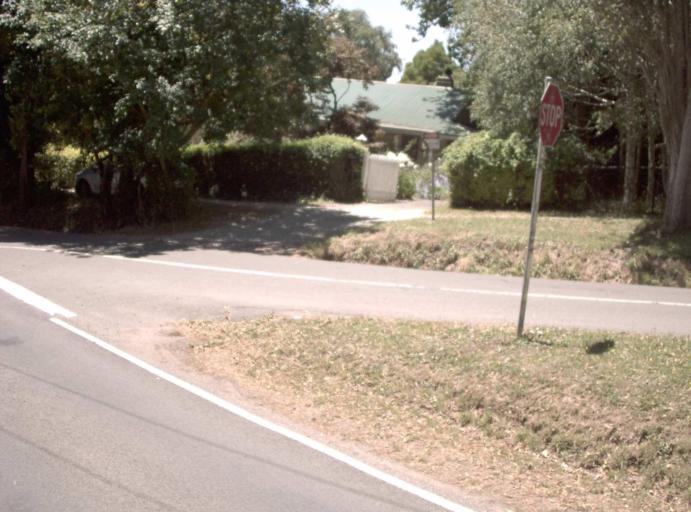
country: AU
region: Victoria
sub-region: Yarra Ranges
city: Olinda
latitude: -37.8501
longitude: 145.3621
